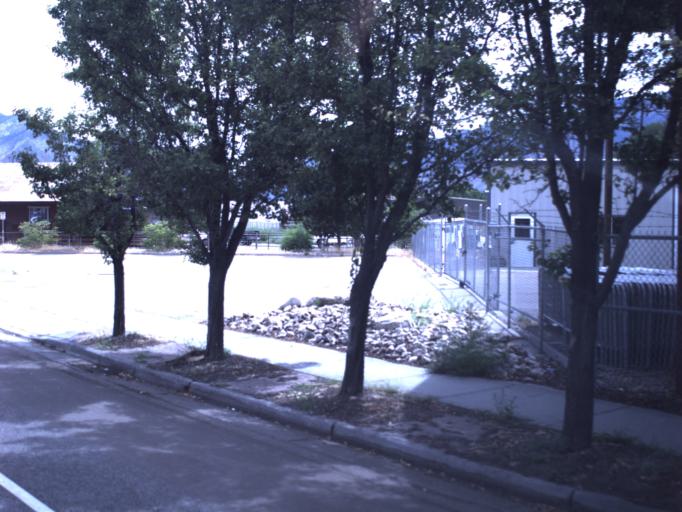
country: US
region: Utah
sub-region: Weber County
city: Ogden
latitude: 41.2222
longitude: -112.0015
